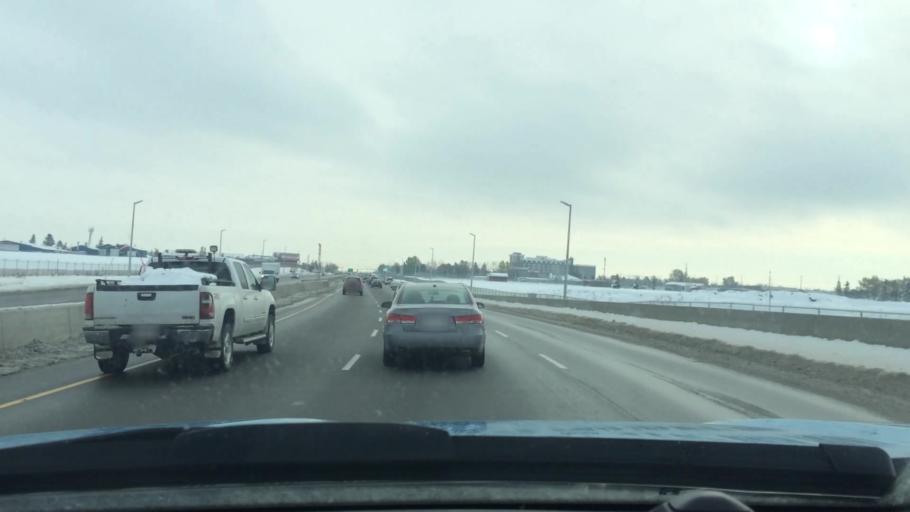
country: CA
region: Alberta
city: Calgary
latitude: 51.0928
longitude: -114.0229
